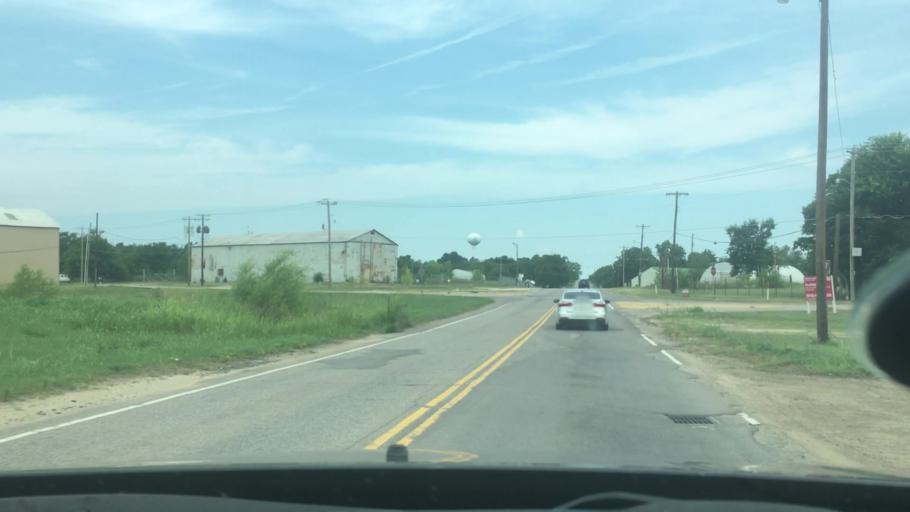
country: US
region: Oklahoma
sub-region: Seminole County
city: Seminole
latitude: 35.2314
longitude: -96.6861
